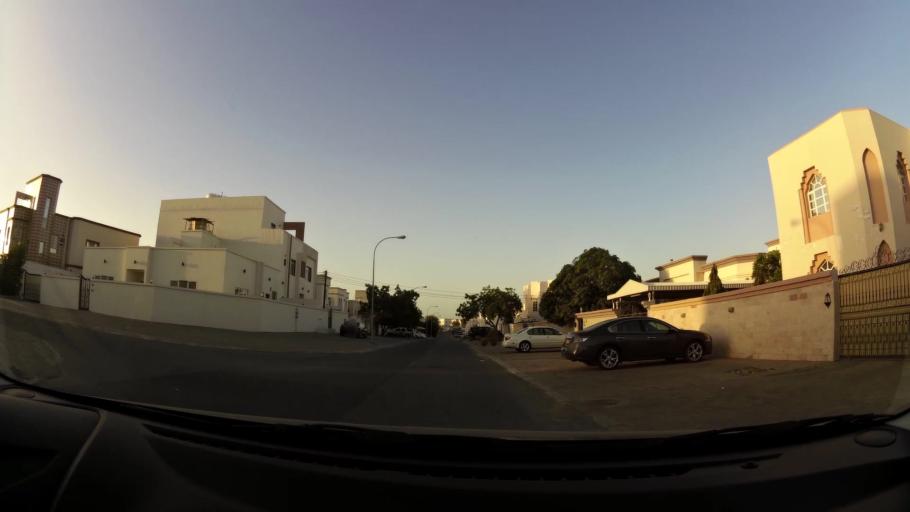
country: OM
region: Muhafazat Masqat
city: As Sib al Jadidah
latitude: 23.6038
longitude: 58.2295
